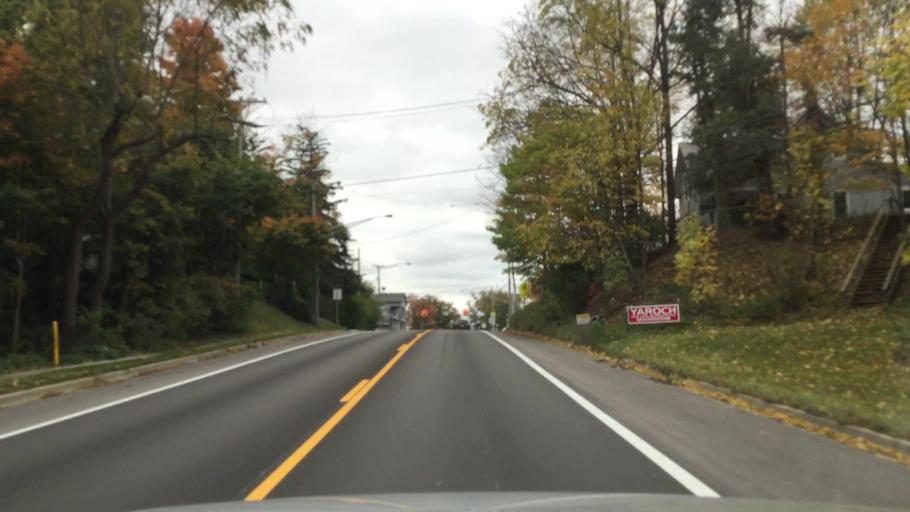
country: US
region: Michigan
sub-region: Macomb County
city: Memphis
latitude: 42.8983
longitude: -82.7692
